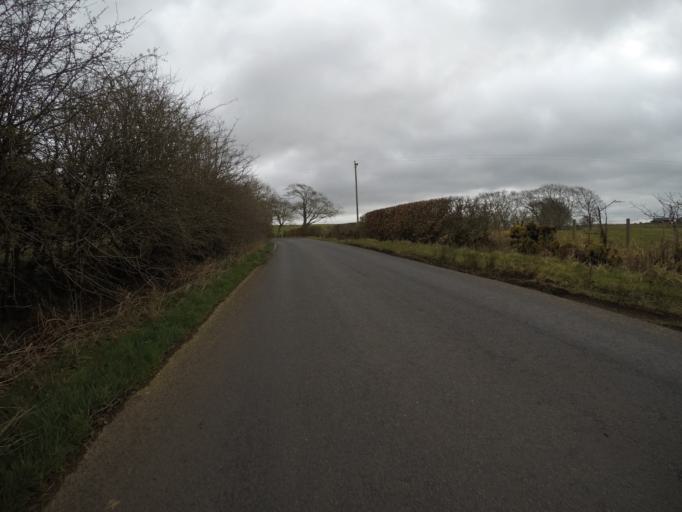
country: GB
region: Scotland
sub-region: East Ayrshire
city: Stewarton
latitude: 55.6801
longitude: -4.4500
